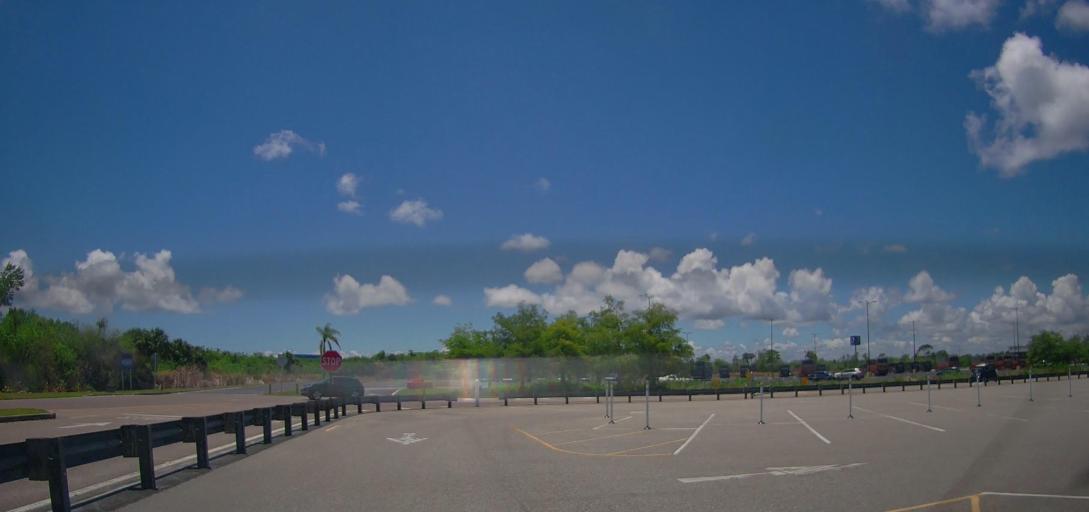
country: US
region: Florida
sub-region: Brevard County
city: Merritt Island
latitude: 28.5206
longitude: -80.6793
